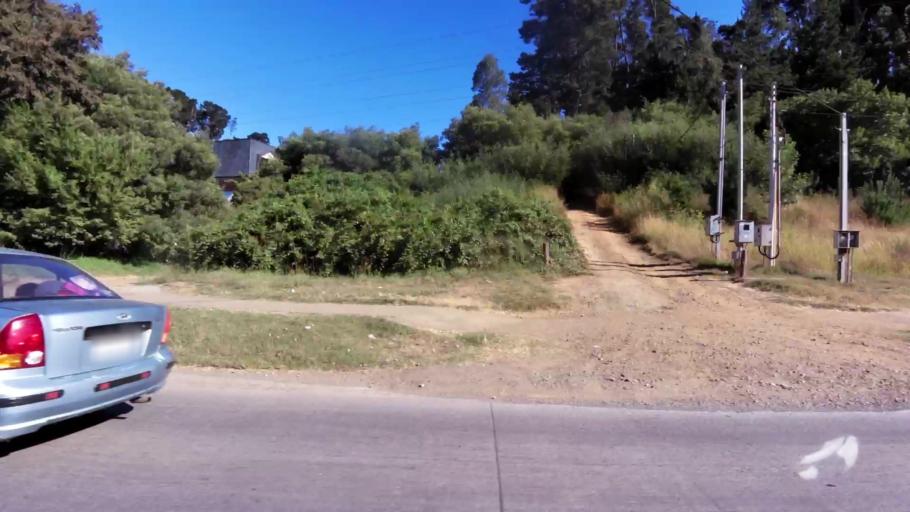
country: CL
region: Biobio
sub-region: Provincia de Concepcion
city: Concepcion
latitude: -36.8433
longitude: -73.1091
